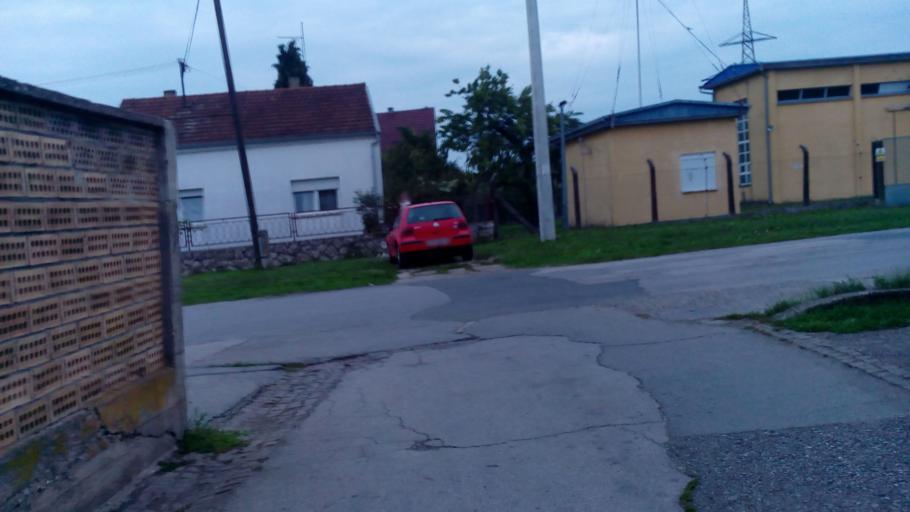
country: HR
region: Vukovarsko-Srijemska
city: Vinkovci
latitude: 45.2799
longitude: 18.8108
